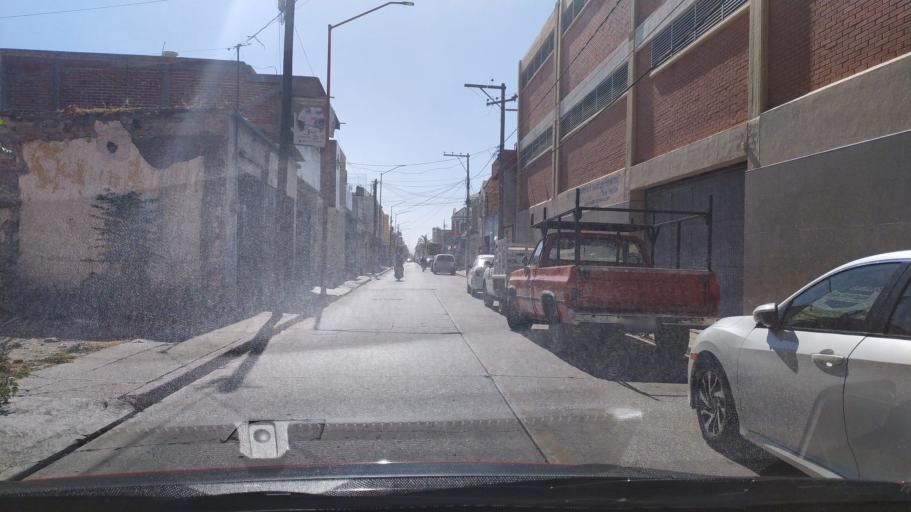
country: MX
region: Guanajuato
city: San Francisco del Rincon
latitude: 21.0249
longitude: -101.8586
